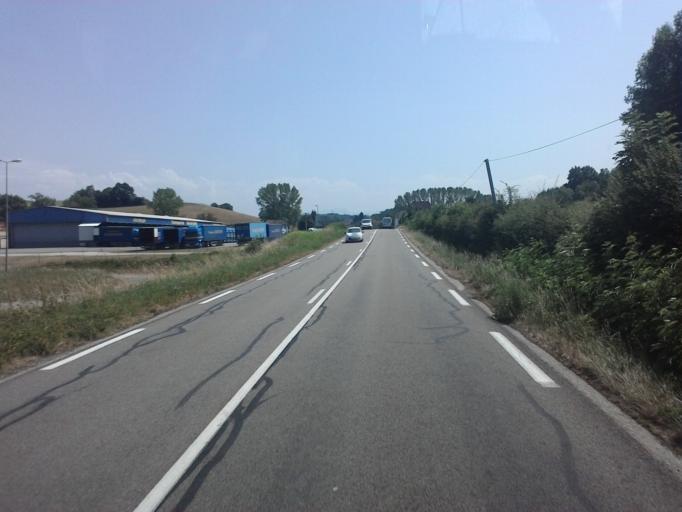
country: FR
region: Rhone-Alpes
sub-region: Departement de l'Isere
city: La Batie-Montgascon
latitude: 45.5906
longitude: 5.5390
